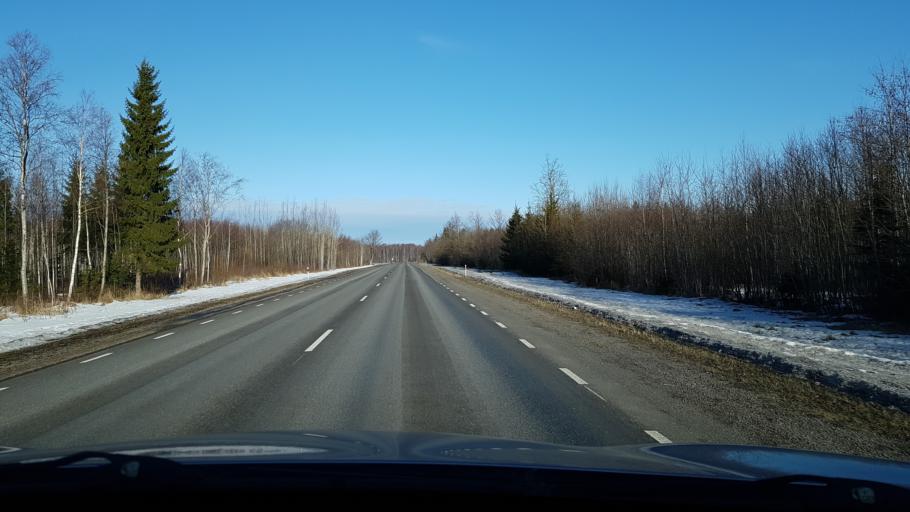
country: EE
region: Viljandimaa
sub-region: Vohma linn
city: Vohma
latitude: 58.6154
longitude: 25.5705
